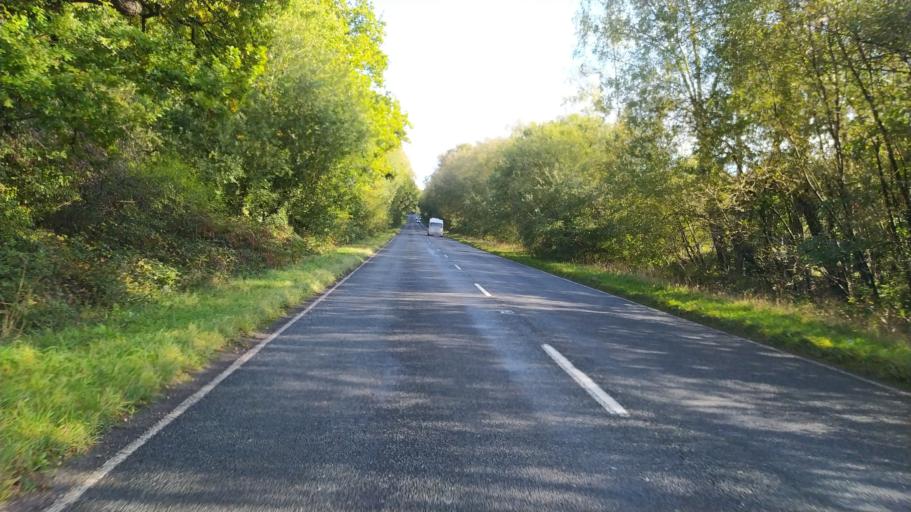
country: GB
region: England
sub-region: Hampshire
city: Lyndhurst
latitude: 50.8625
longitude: -1.5993
